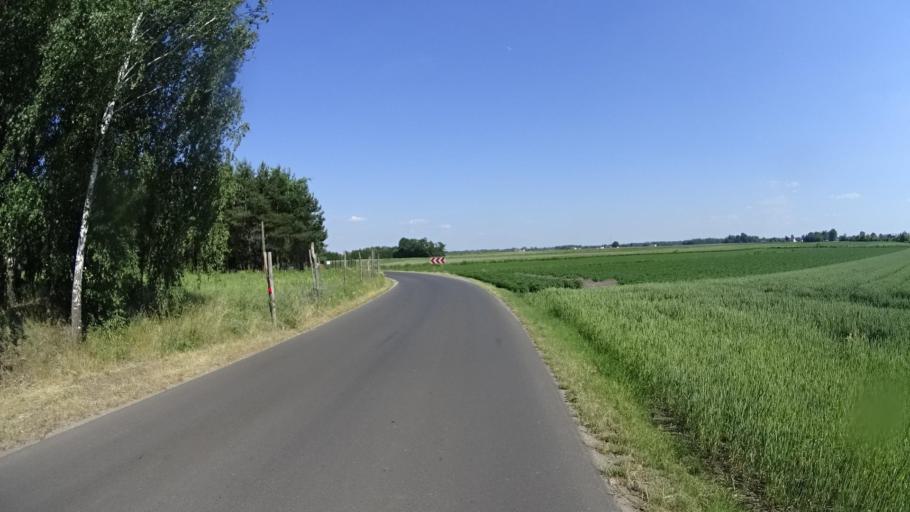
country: PL
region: Masovian Voivodeship
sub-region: Powiat warszawski zachodni
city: Blonie
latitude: 52.1637
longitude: 20.6382
